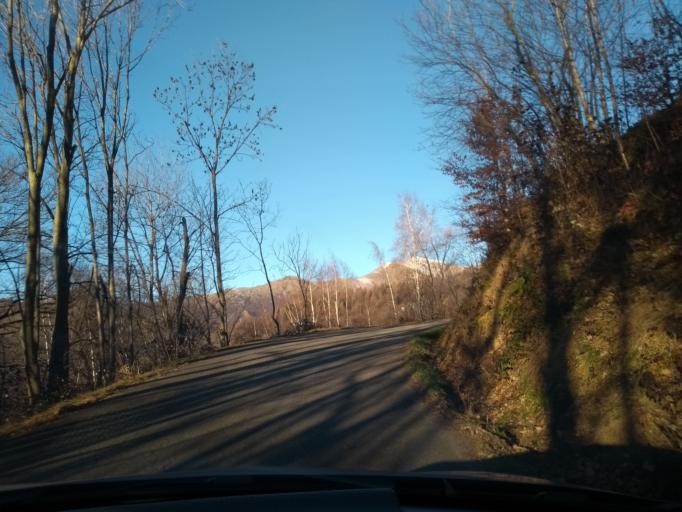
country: IT
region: Piedmont
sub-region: Provincia di Torino
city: Corio
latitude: 45.3274
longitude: 7.5449
